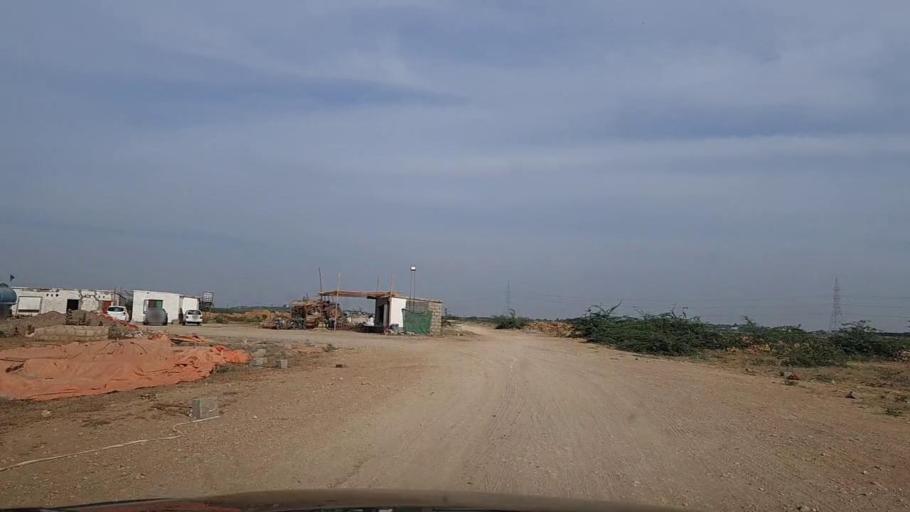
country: PK
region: Sindh
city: Gharo
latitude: 24.7738
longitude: 67.5462
